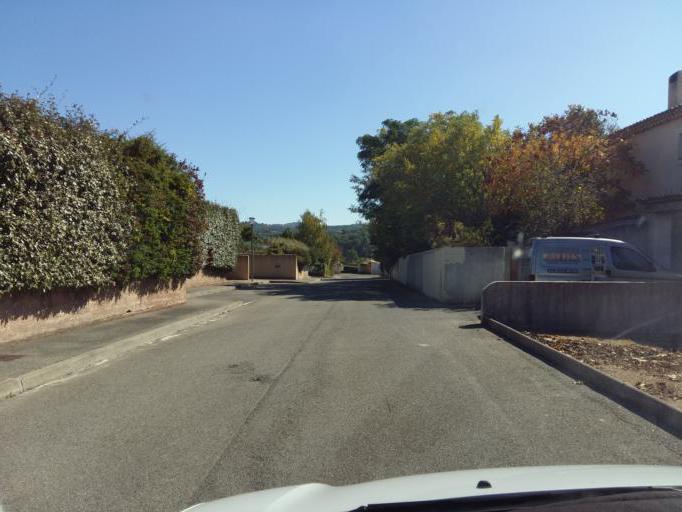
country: FR
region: Provence-Alpes-Cote d'Azur
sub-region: Departement du Vaucluse
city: Pertuis
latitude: 43.7218
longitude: 5.5393
